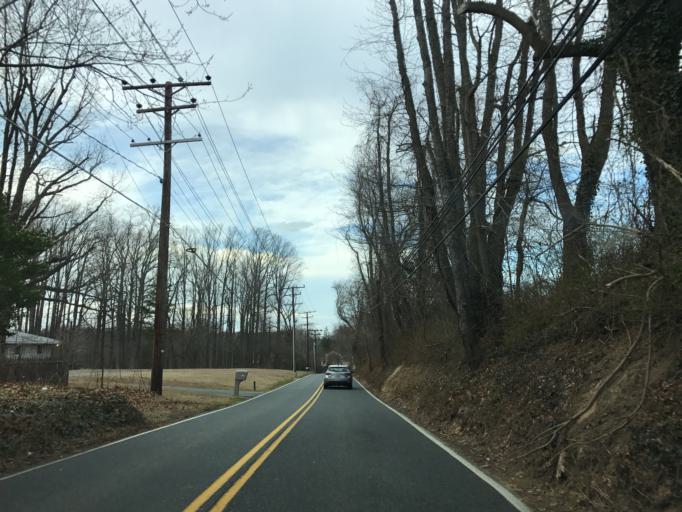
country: US
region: Maryland
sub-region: Harford County
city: South Bel Air
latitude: 39.5458
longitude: -76.2874
